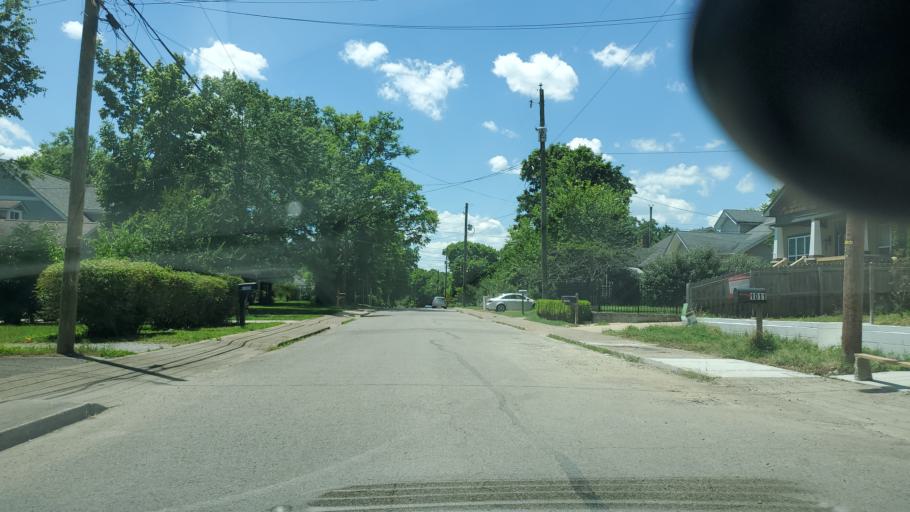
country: US
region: Tennessee
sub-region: Davidson County
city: Nashville
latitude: 36.1897
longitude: -86.7493
